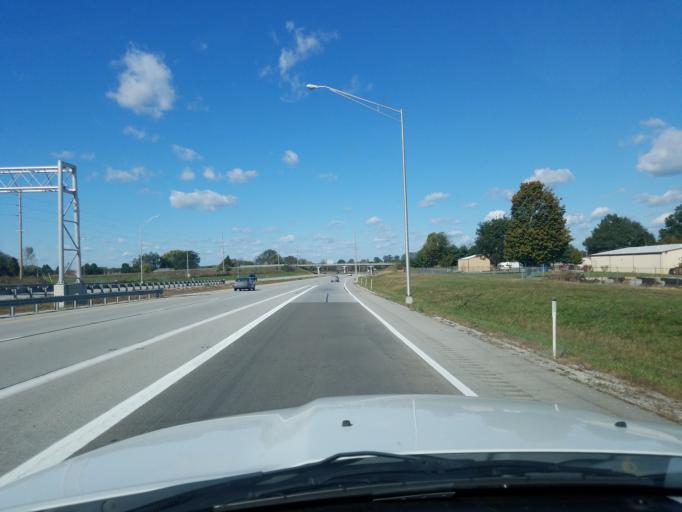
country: US
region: Kentucky
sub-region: Warren County
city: Plano
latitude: 36.9123
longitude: -86.4366
